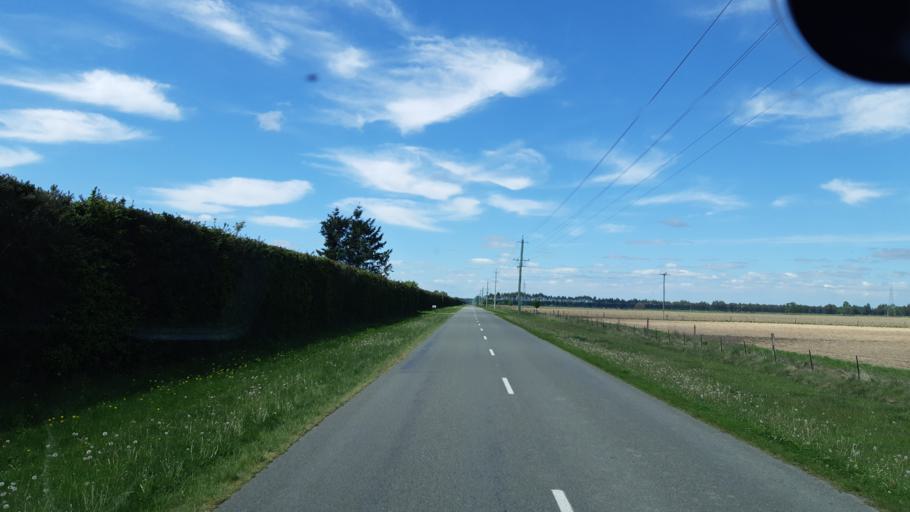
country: NZ
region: Canterbury
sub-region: Ashburton District
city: Methven
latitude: -43.7222
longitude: 171.4764
